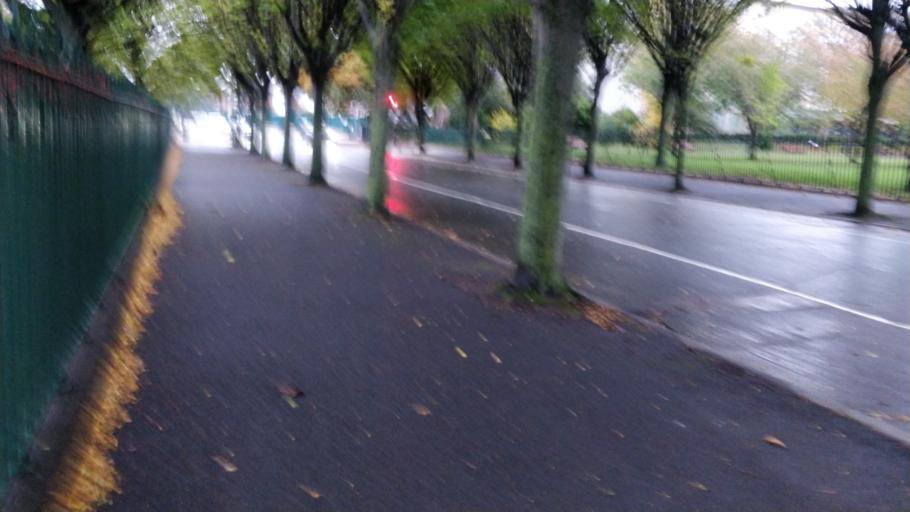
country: IE
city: Clonskeagh
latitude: 53.3280
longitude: -6.2348
